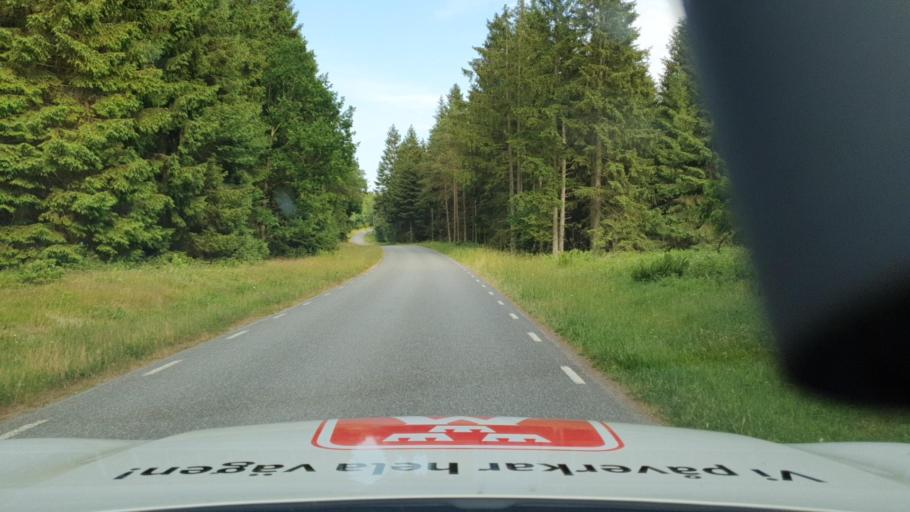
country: SE
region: Skane
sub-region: Kristianstads Kommun
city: Degeberga
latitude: 55.6923
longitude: 14.0756
